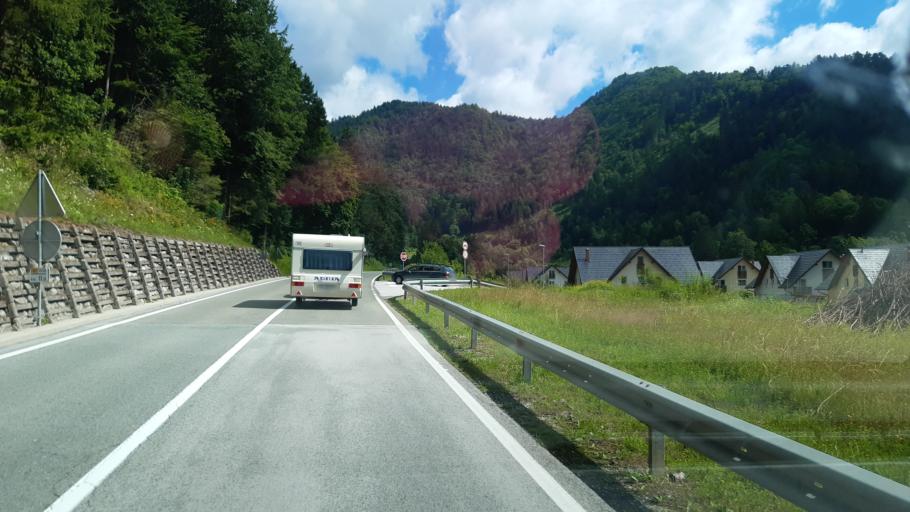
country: SI
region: Trzic
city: Trzic
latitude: 46.3647
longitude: 14.3058
